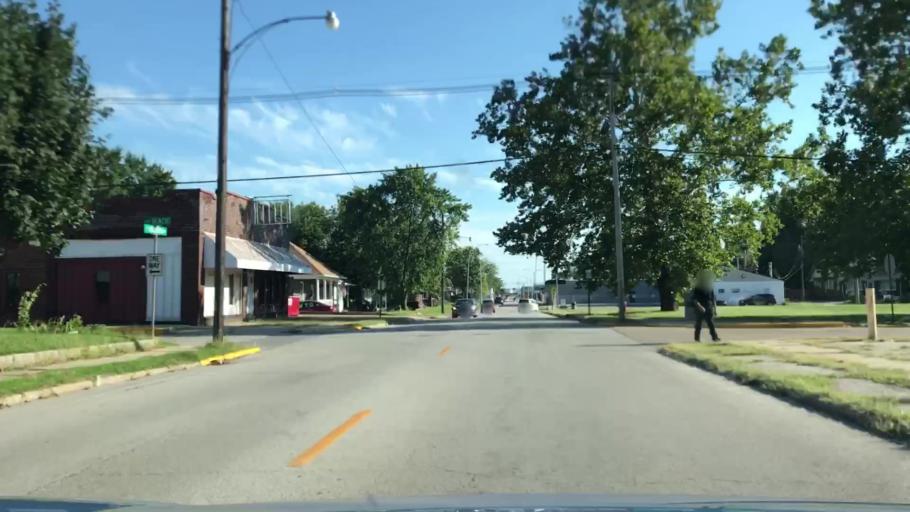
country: US
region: Illinois
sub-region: Madison County
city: Wood River
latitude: 38.8664
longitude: -90.0985
